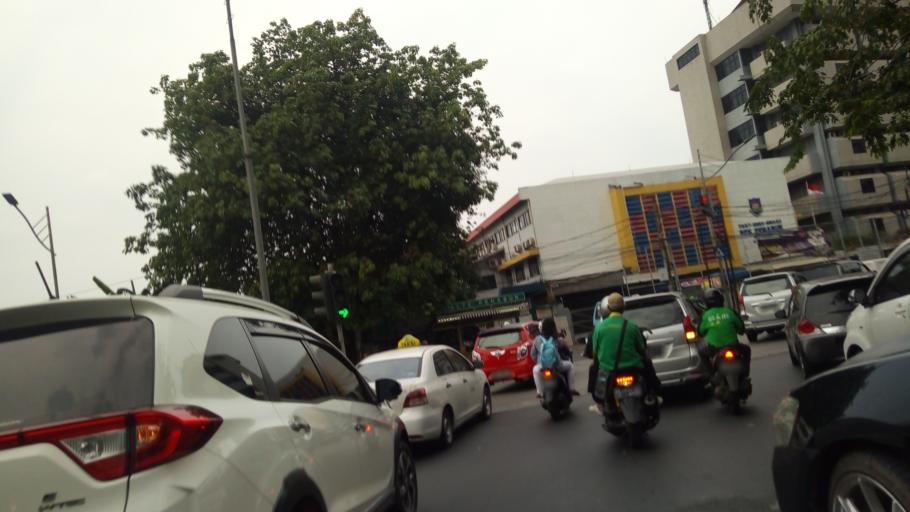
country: ID
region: Jakarta Raya
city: Jakarta
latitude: -6.1698
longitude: 106.8397
